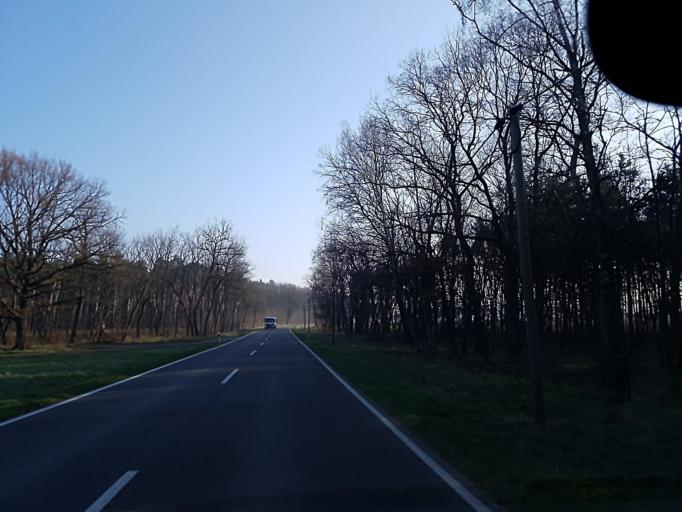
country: DE
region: Brandenburg
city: Bronkow
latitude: 51.6579
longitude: 13.9008
